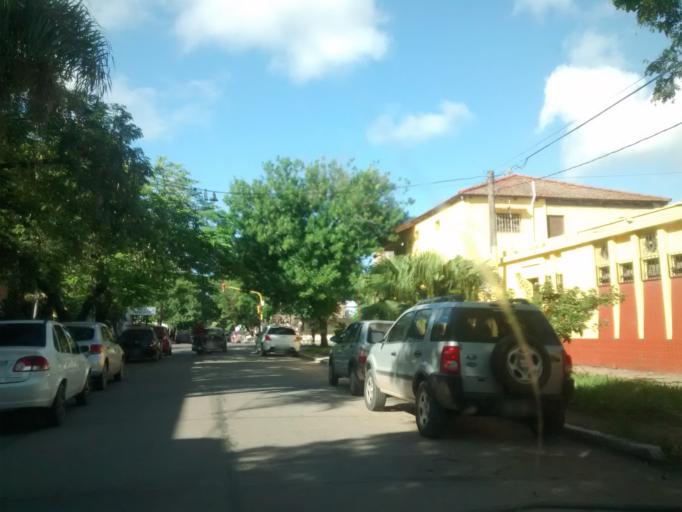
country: AR
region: Chaco
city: Resistencia
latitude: -27.4562
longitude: -58.9799
